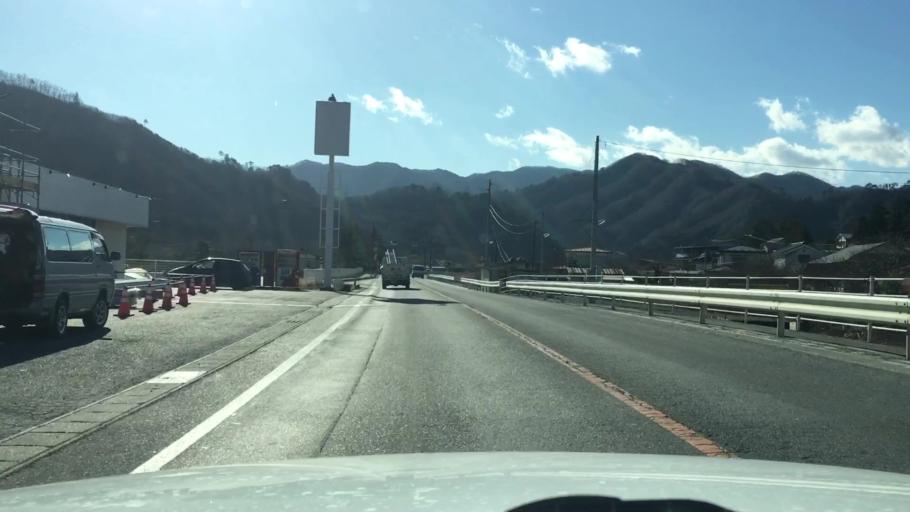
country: JP
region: Iwate
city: Miyako
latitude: 39.6309
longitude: 141.8620
